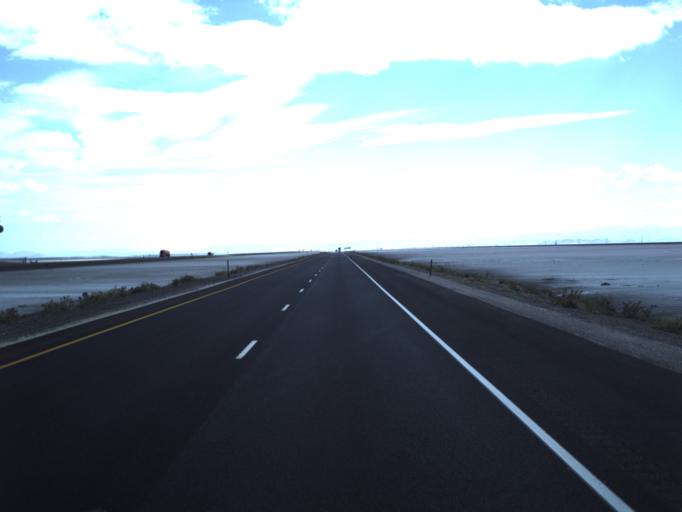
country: US
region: Utah
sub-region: Tooele County
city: Wendover
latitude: 40.7322
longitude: -113.5567
